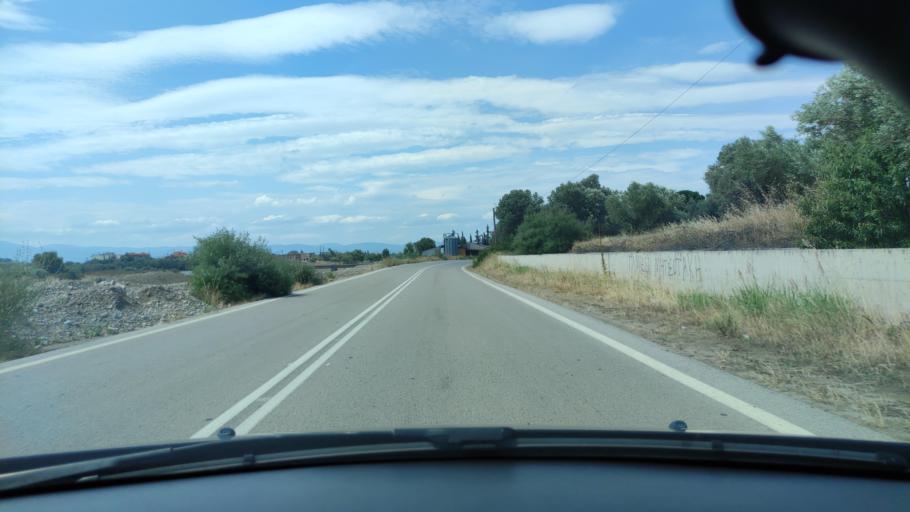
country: GR
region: Central Greece
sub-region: Nomos Evvoias
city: Afration
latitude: 38.4551
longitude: 23.6806
